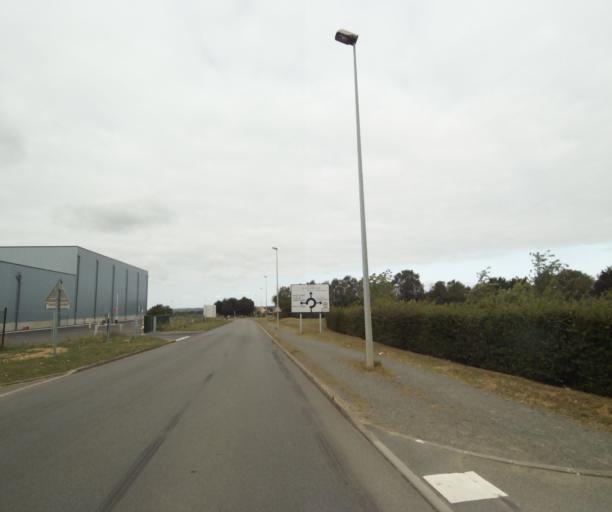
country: FR
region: Pays de la Loire
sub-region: Departement de la Sarthe
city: Sable-sur-Sarthe
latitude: 47.8262
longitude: -0.3163
